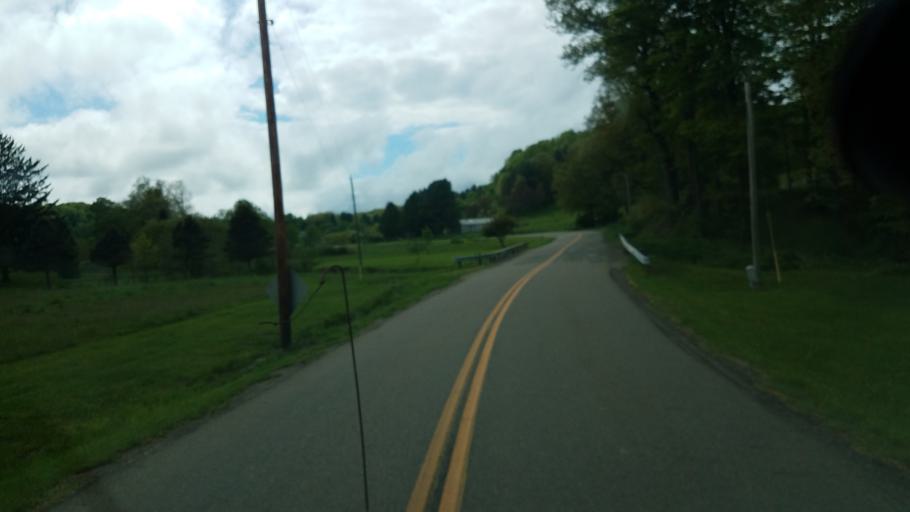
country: US
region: Ohio
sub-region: Tuscarawas County
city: Strasburg
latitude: 40.6378
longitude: -81.4876
